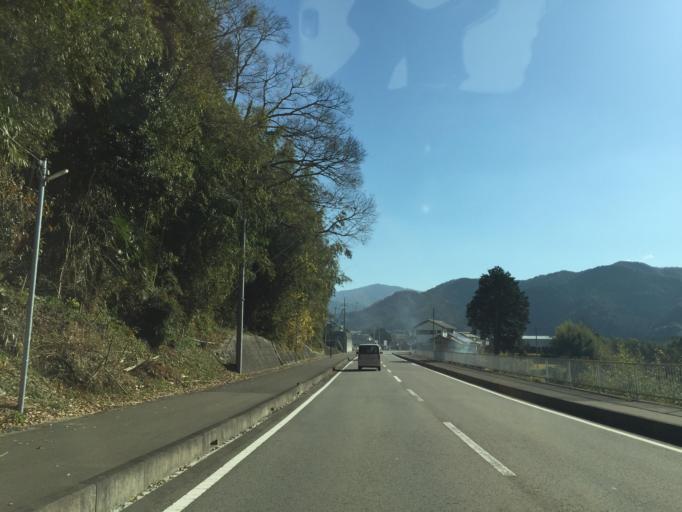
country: JP
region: Wakayama
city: Iwade
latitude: 34.1614
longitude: 135.3091
